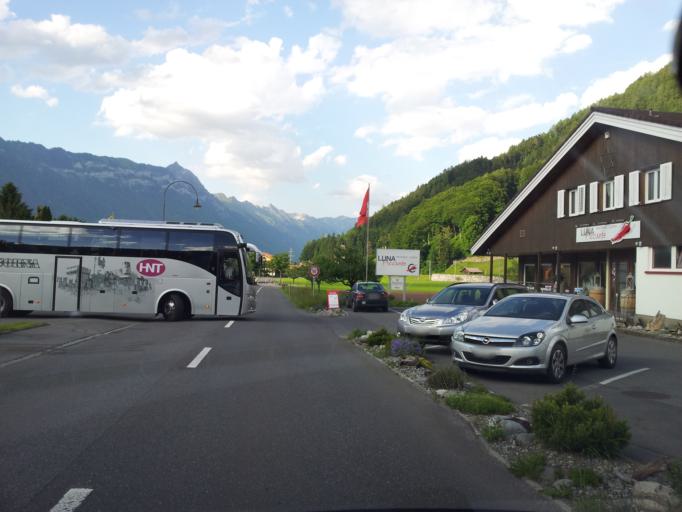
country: CH
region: Bern
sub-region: Interlaken-Oberhasli District
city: Wilderswil
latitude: 46.6611
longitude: 7.8671
